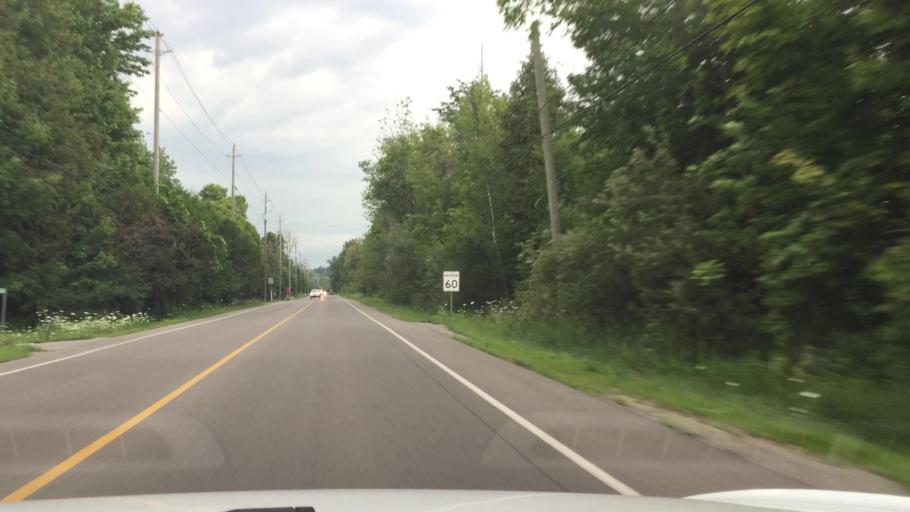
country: CA
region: Ontario
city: Oshawa
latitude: 43.9245
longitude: -78.7944
